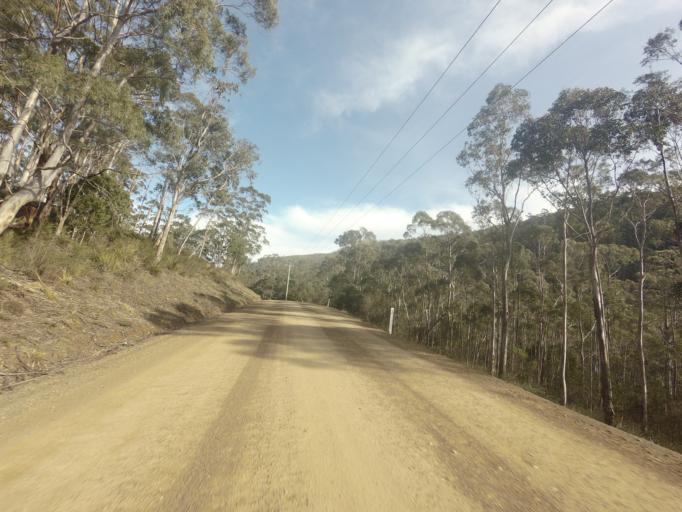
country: AU
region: Tasmania
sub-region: Huon Valley
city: Huonville
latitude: -43.0533
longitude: 147.1025
